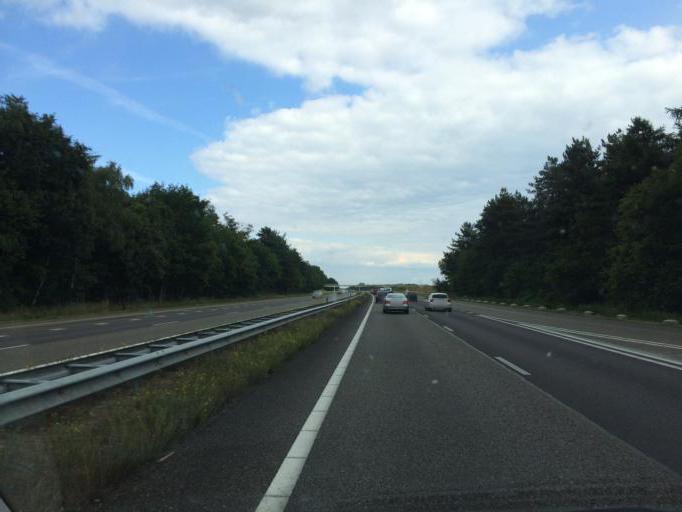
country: NL
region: North Brabant
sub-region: Gemeente Asten
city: Asten
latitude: 51.4038
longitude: 5.8145
